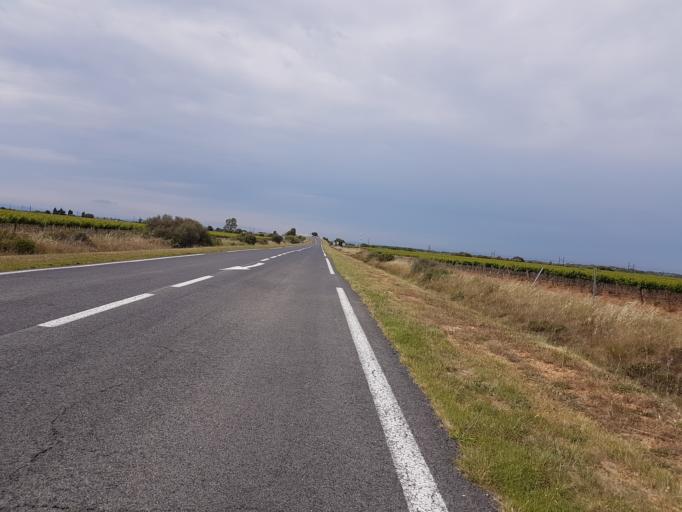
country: FR
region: Languedoc-Roussillon
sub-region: Departement de l'Herault
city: Portiragnes
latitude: 43.3155
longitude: 3.3605
